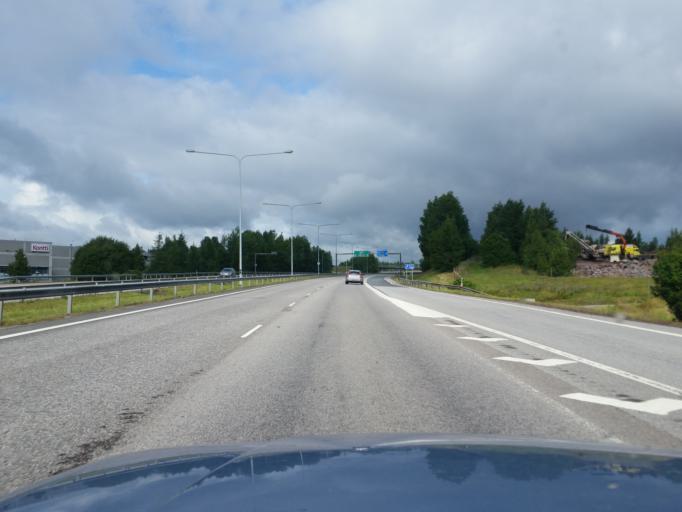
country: FI
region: Uusimaa
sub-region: Helsinki
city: Espoo
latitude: 60.2165
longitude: 24.6577
